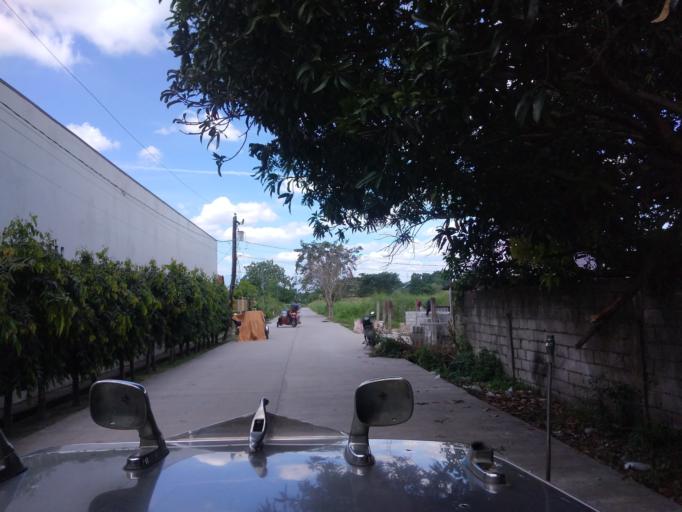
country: PH
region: Central Luzon
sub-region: Province of Pampanga
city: Santa Rita
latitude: 15.0082
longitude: 120.5925
